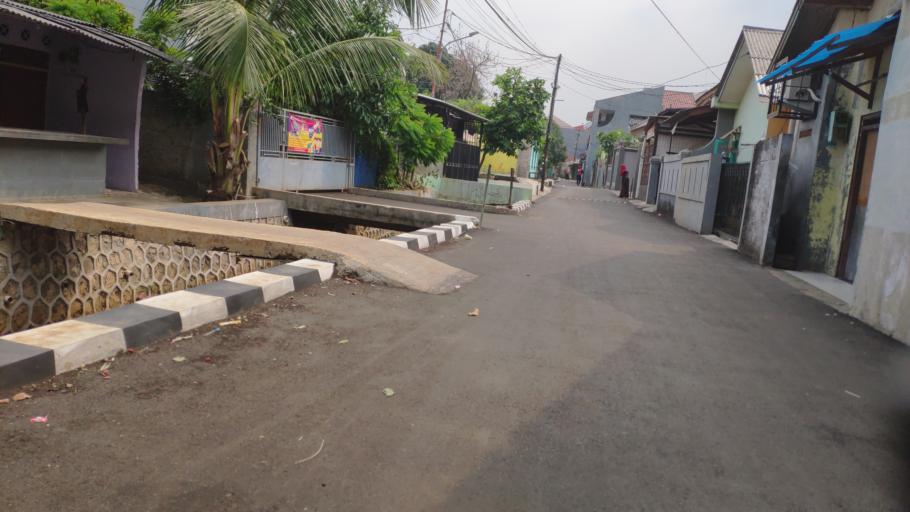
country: ID
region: West Java
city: Depok
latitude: -6.3448
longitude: 106.8147
